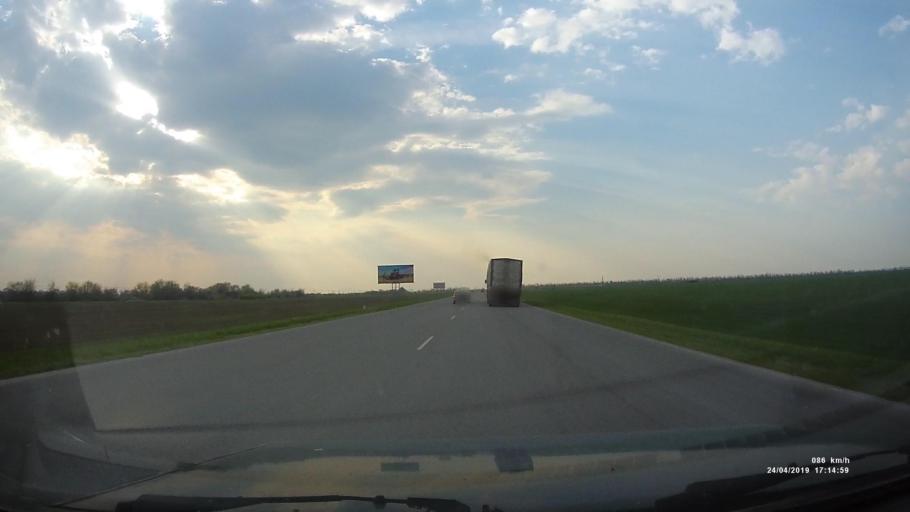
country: RU
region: Rostov
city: Sal'sk
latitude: 46.4855
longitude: 41.4497
